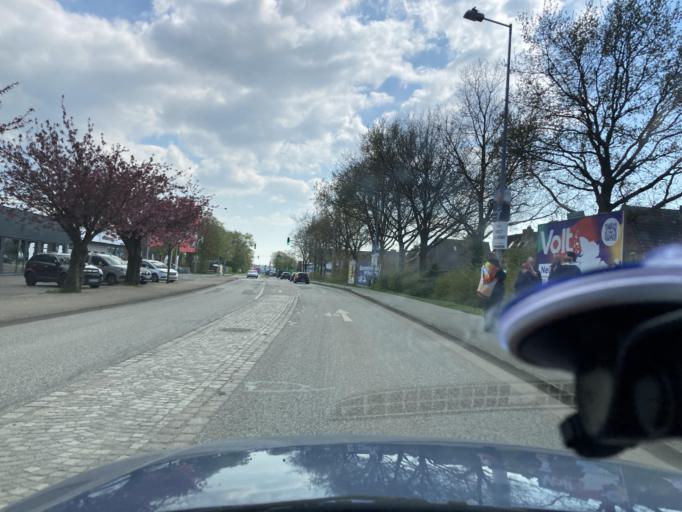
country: DE
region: Schleswig-Holstein
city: Heide
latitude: 54.1816
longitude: 9.0903
